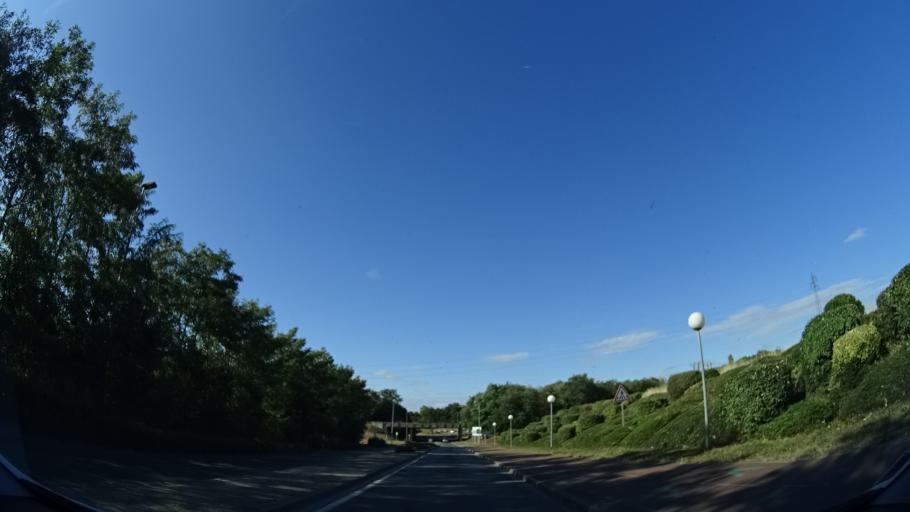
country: FR
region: Centre
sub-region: Departement du Loiret
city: Semoy
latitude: 47.9224
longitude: 1.9567
